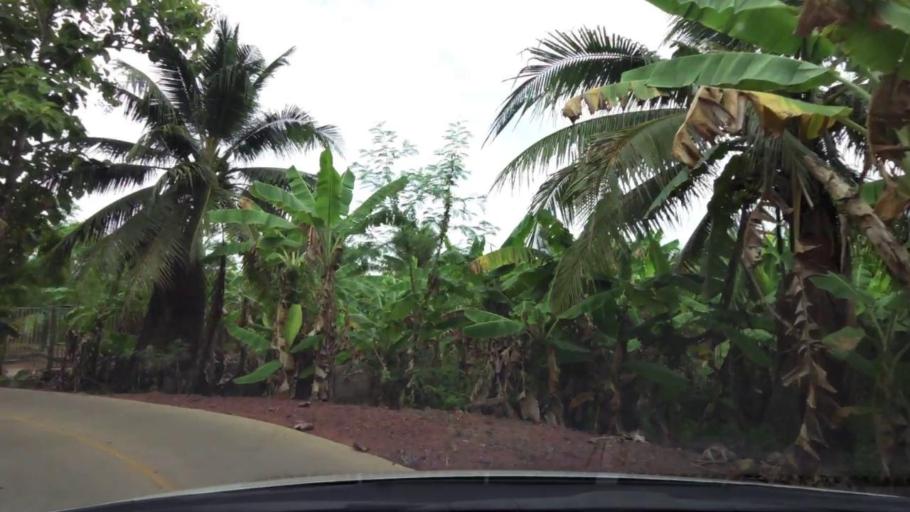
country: TH
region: Ratchaburi
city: Damnoen Saduak
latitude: 13.5522
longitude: 99.9715
